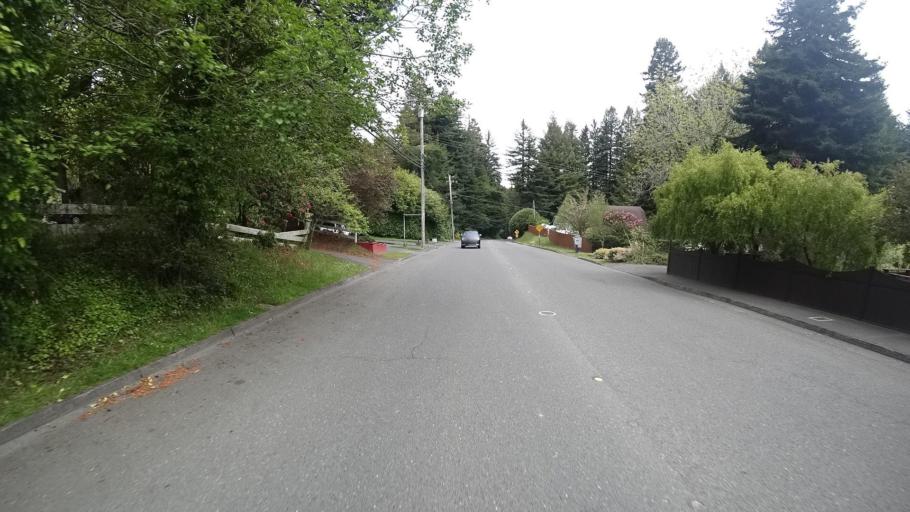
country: US
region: California
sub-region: Humboldt County
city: Cutten
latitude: 40.7645
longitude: -124.1548
